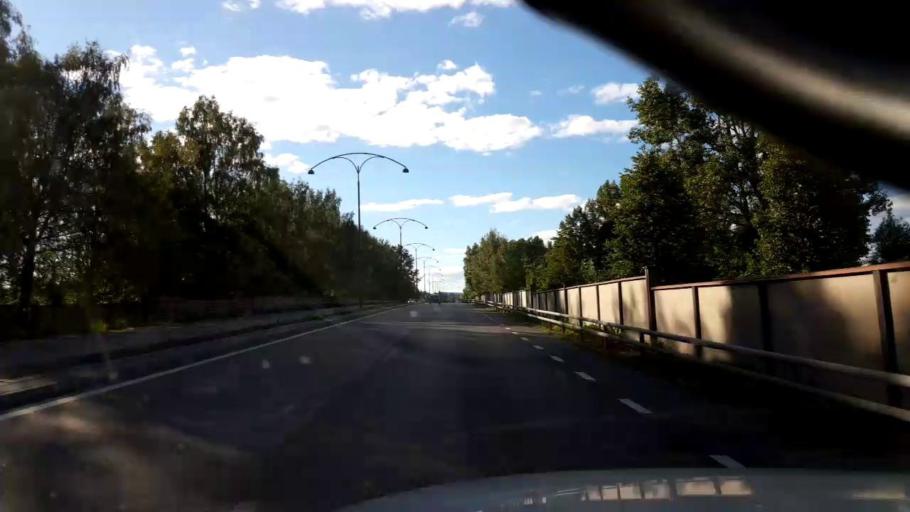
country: SE
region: Dalarna
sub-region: Borlange Kommun
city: Borlaenge
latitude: 60.4773
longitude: 15.4524
